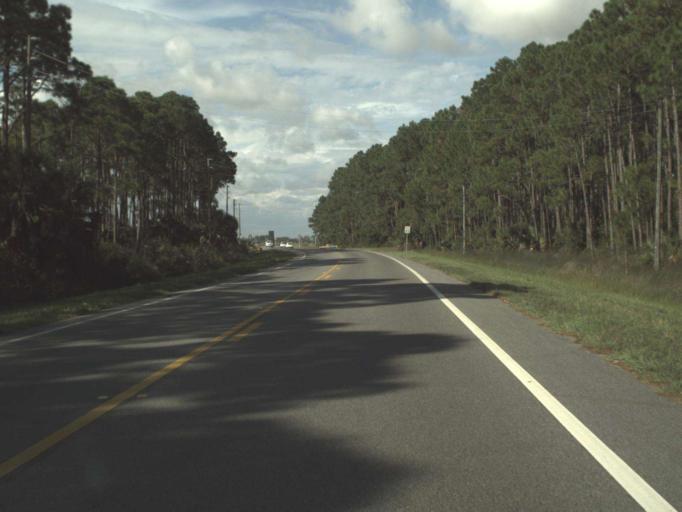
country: US
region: Florida
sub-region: Gulf County
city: Port Saint Joe
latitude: 29.7868
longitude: -85.3013
